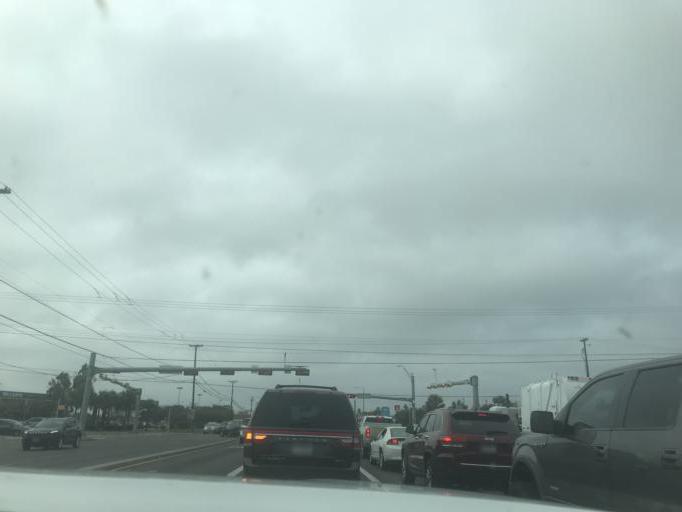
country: US
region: Texas
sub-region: Nueces County
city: Corpus Christi
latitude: 27.6852
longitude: -97.3832
